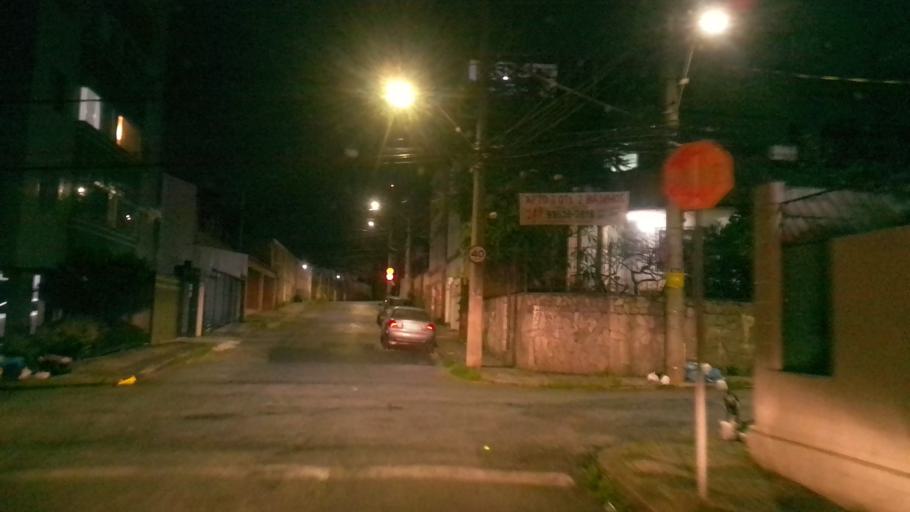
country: BR
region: Minas Gerais
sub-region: Belo Horizonte
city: Belo Horizonte
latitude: -19.9121
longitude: -43.9591
